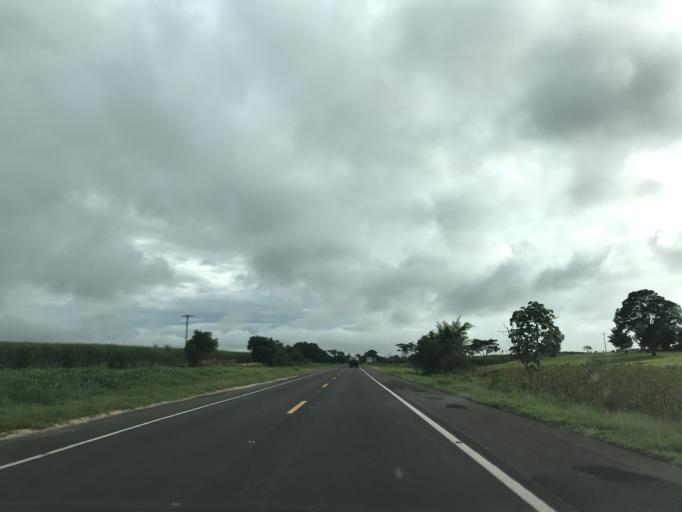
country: BR
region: Sao Paulo
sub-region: Penapolis
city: Penapolis
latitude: -21.4670
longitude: -50.1835
